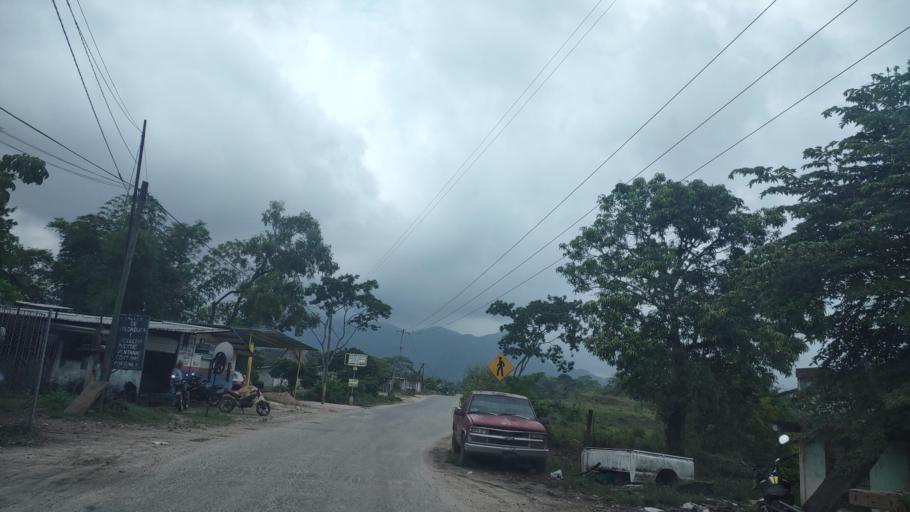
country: MX
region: Veracruz
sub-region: Uxpanapa
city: Poblado 10
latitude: 17.5001
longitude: -94.1627
